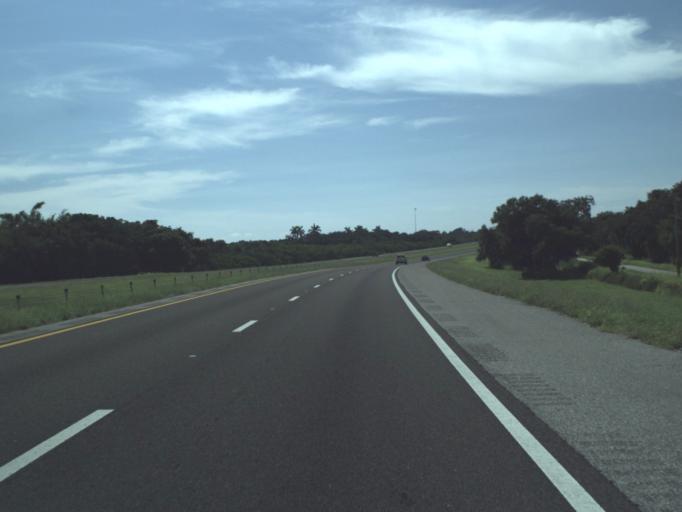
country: US
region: Florida
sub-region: Manatee County
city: Memphis
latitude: 27.5805
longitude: -82.5686
